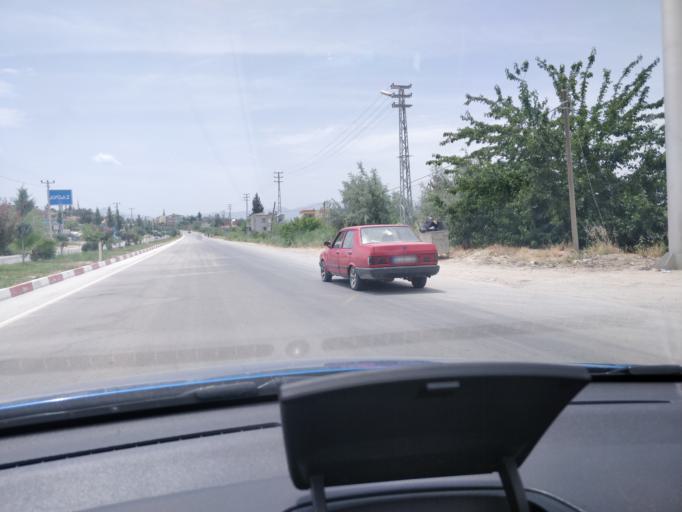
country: TR
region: Mersin
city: Mut
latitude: 36.6226
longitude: 33.4435
